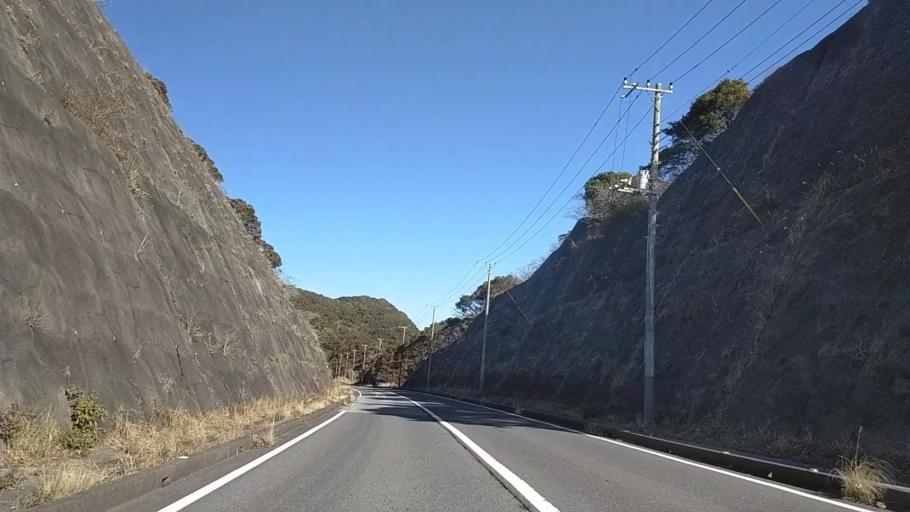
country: JP
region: Chiba
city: Katsuura
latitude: 35.1271
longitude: 140.2370
